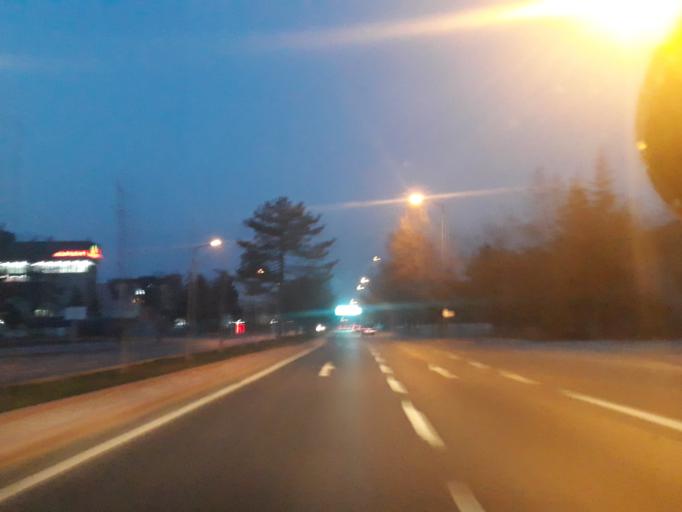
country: TR
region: Konya
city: Selcuklu
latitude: 37.9028
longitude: 32.5108
